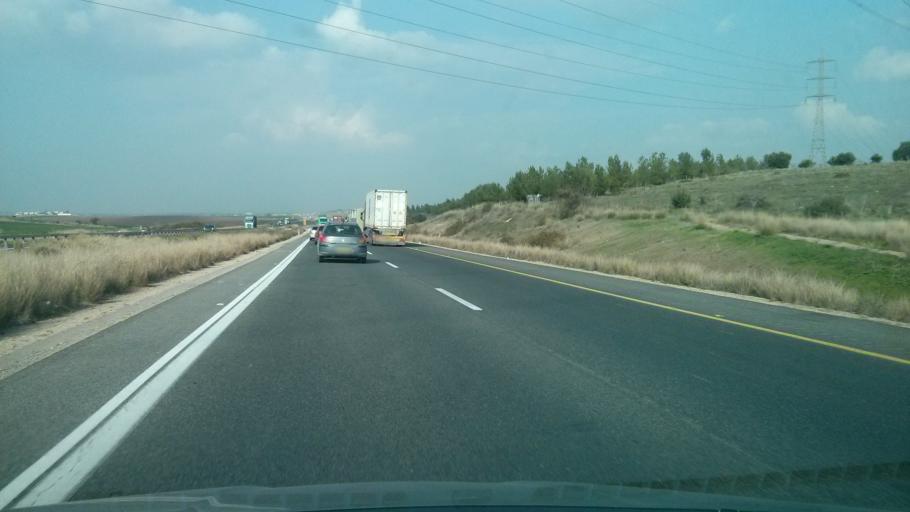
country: IL
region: Southern District
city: Qiryat Gat
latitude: 31.6866
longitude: 34.8104
